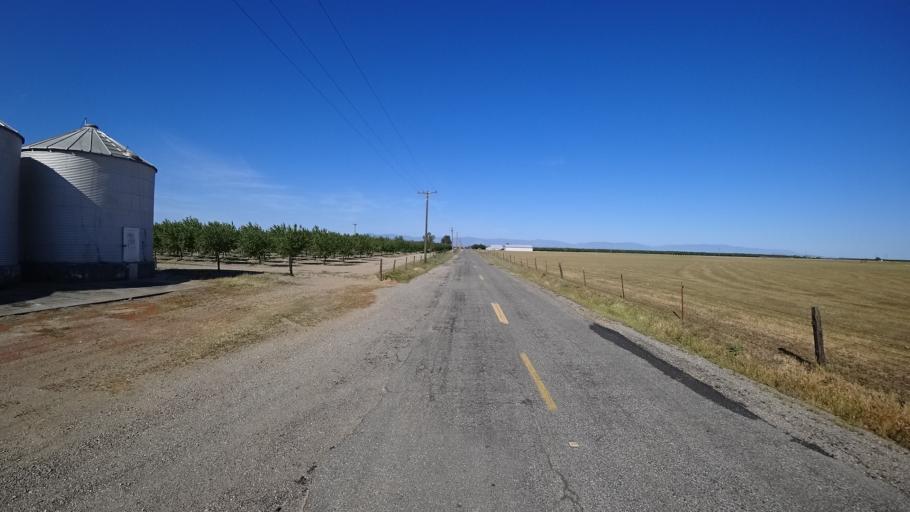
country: US
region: California
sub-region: Glenn County
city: Willows
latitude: 39.6112
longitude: -122.1522
